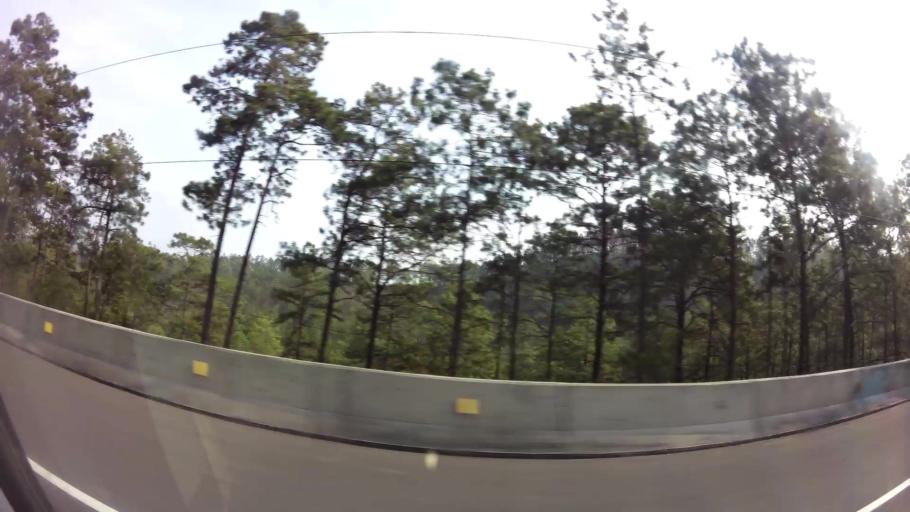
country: HN
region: Francisco Morazan
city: Zambrano
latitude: 14.2855
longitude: -87.4507
